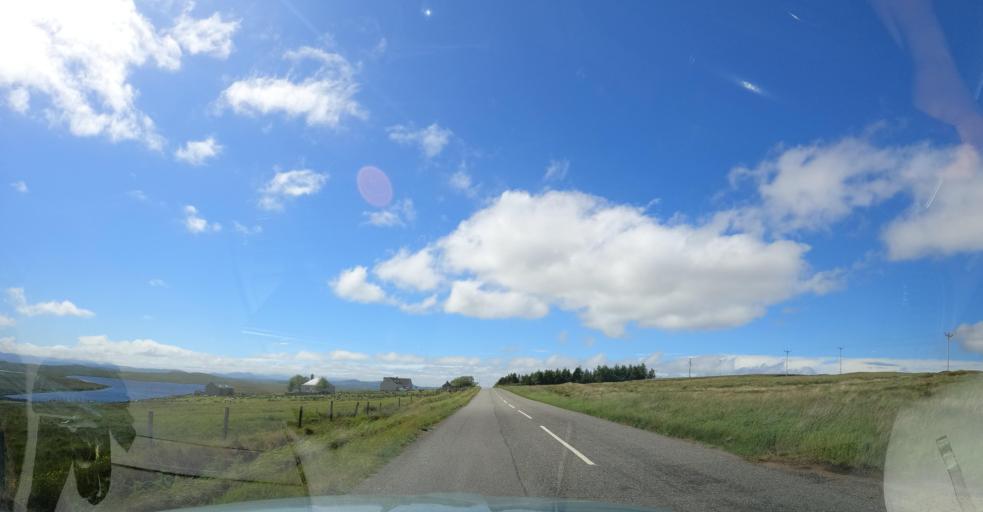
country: GB
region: Scotland
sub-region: Eilean Siar
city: Stornoway
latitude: 58.1741
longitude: -6.6046
